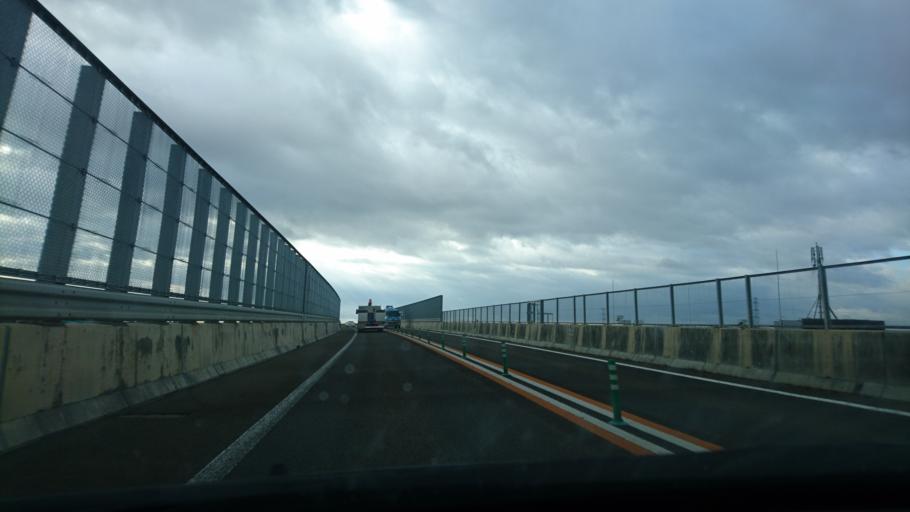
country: JP
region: Miyagi
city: Rifu
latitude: 38.3197
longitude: 140.9675
